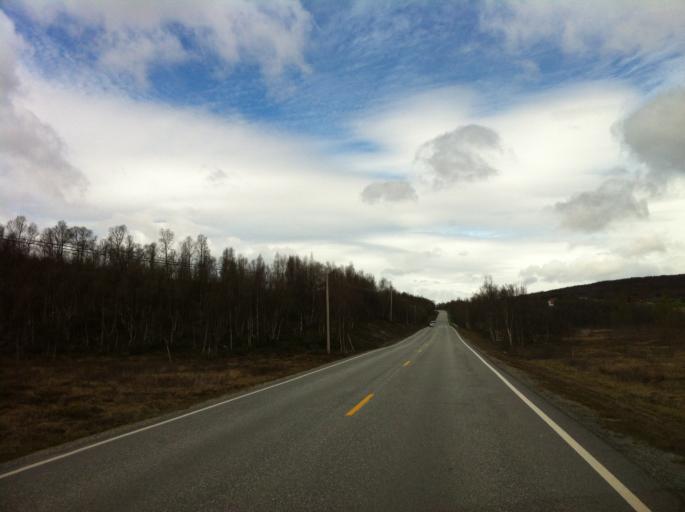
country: NO
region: Sor-Trondelag
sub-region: Roros
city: Roros
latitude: 62.5941
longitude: 11.7674
